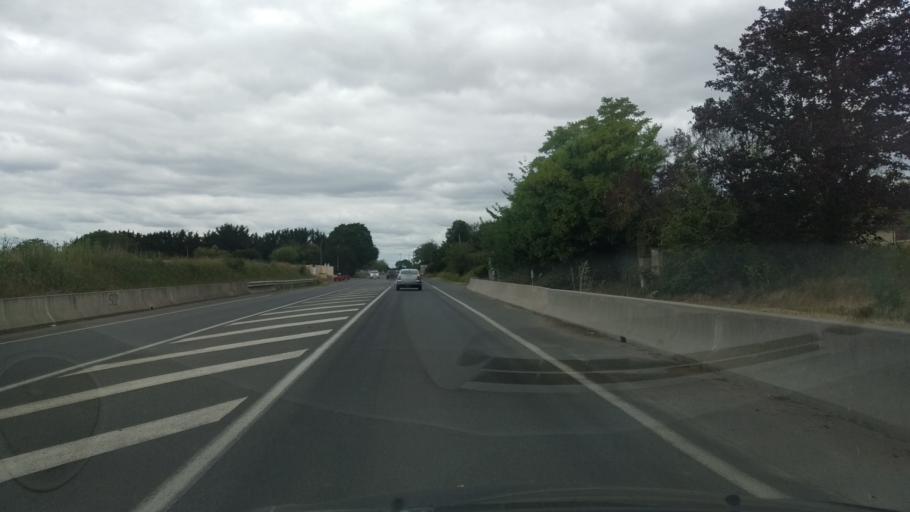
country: FR
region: Poitou-Charentes
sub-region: Departement de la Vienne
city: Biard
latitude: 46.6027
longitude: 0.3134
